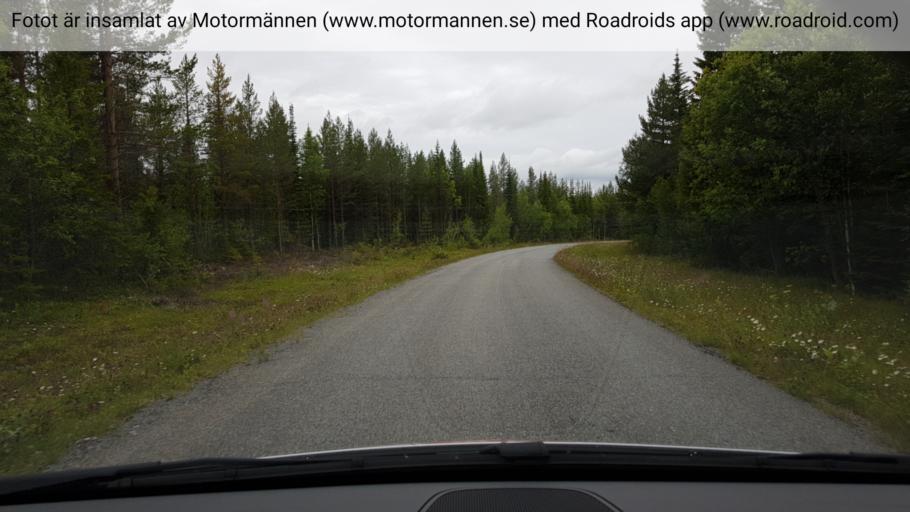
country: SE
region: Jaemtland
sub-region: Krokoms Kommun
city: Krokom
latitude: 63.7565
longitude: 14.4161
